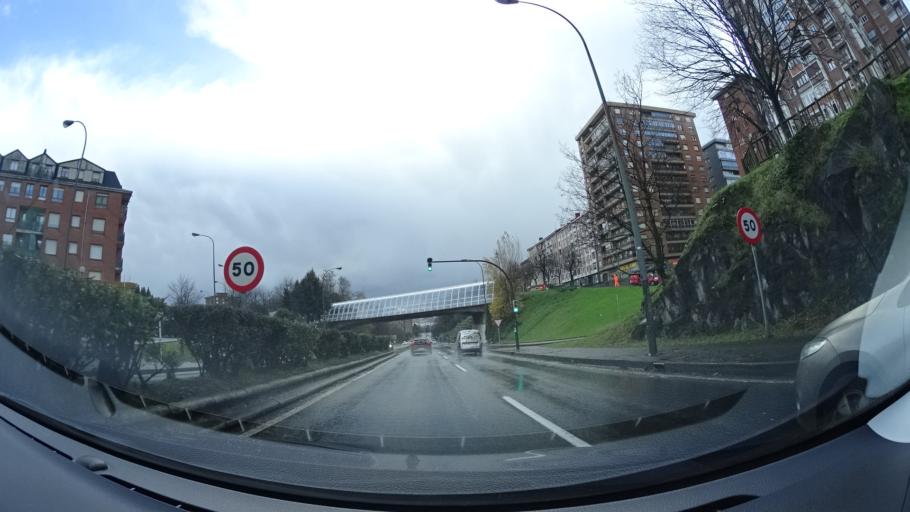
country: ES
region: Basque Country
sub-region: Bizkaia
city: Santutxu
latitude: 43.2555
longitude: -2.9105
